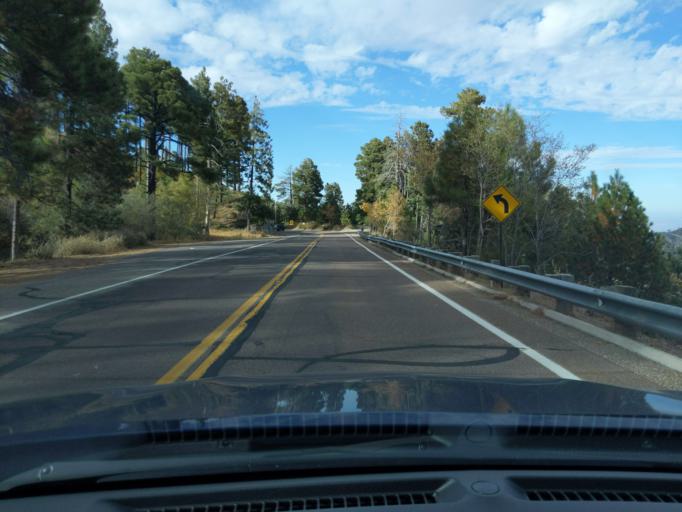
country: US
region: Arizona
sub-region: Pinal County
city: Oracle
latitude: 32.4463
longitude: -110.7532
